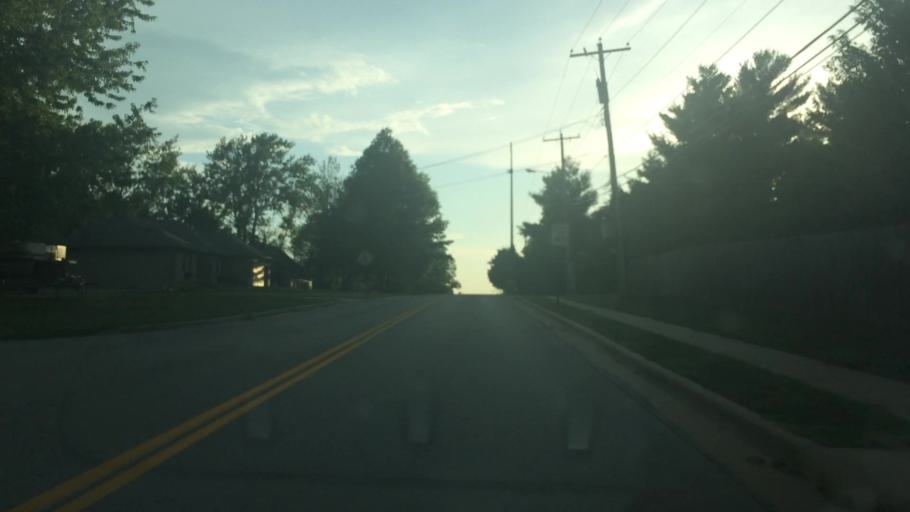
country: US
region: Missouri
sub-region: Greene County
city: Strafford
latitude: 37.2013
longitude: -93.1905
